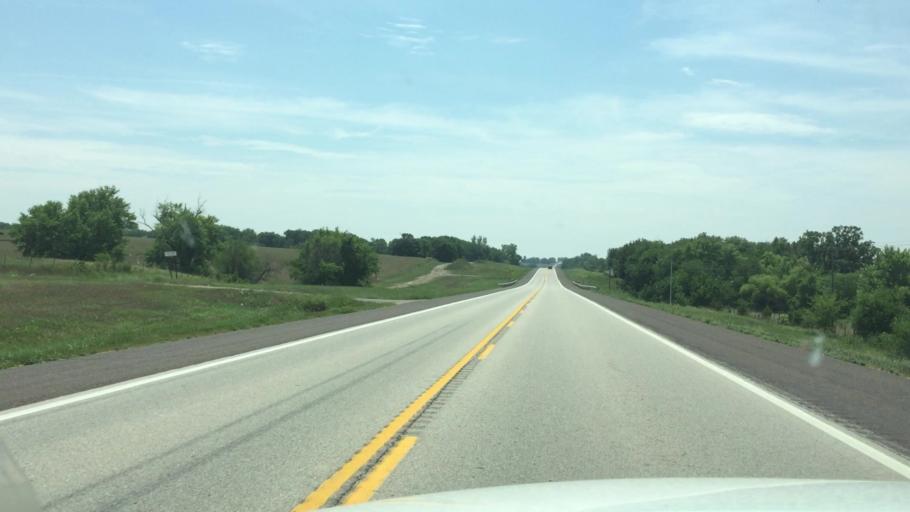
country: US
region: Kansas
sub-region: Jackson County
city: Holton
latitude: 39.5932
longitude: -95.7319
